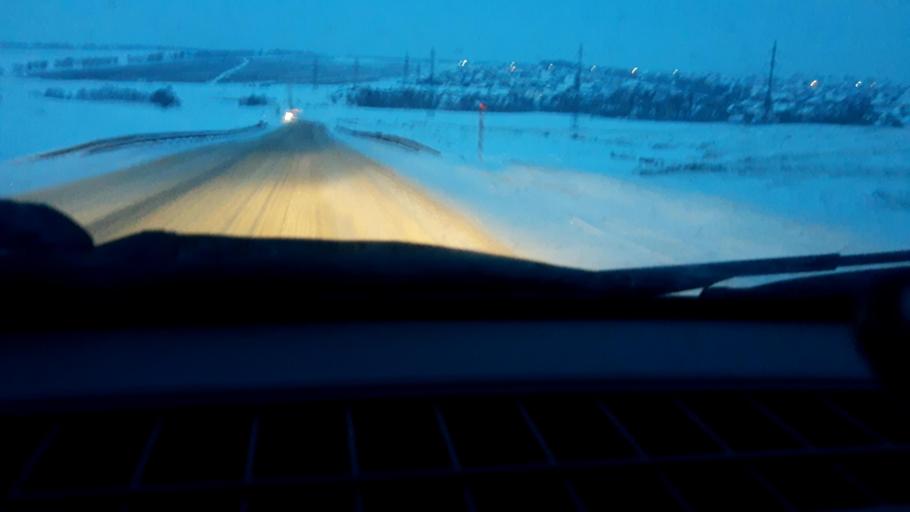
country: RU
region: Bashkortostan
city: Alekseyevka
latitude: 54.6786
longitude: 55.0139
